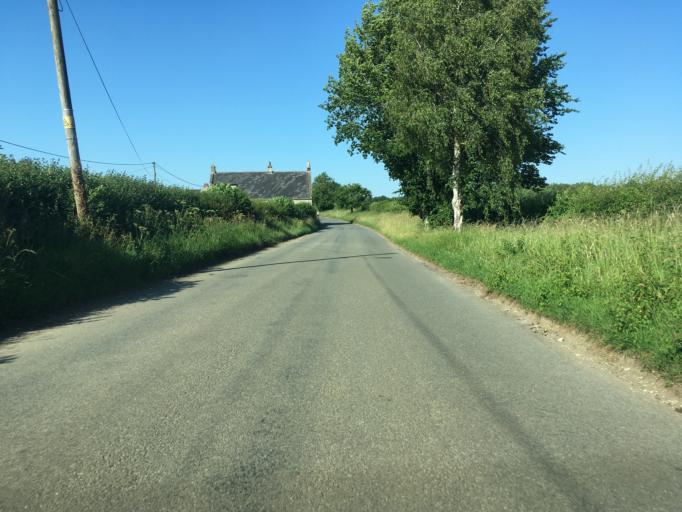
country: GB
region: England
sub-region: South Gloucestershire
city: Pucklechurch
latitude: 51.4608
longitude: -2.4086
